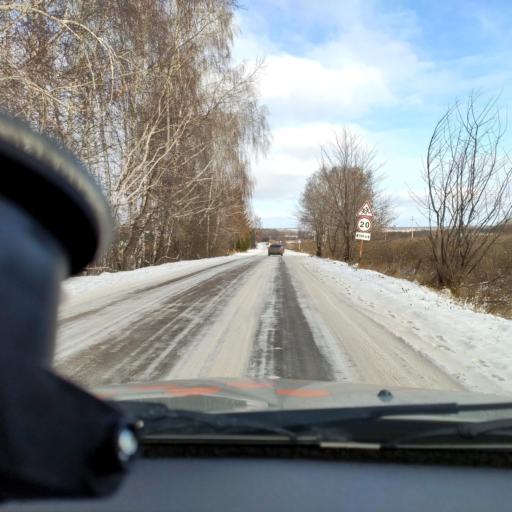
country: RU
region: Bashkortostan
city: Avdon
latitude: 54.7827
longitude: 55.7580
